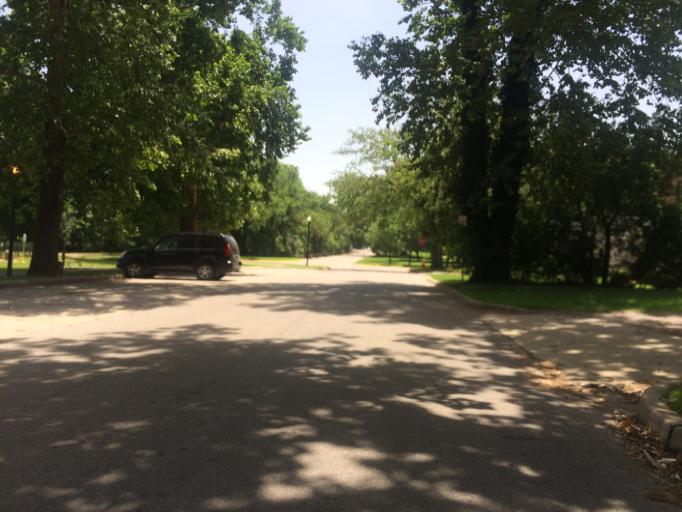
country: US
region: Oklahoma
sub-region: Cleveland County
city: Norman
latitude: 35.2136
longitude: -97.4547
